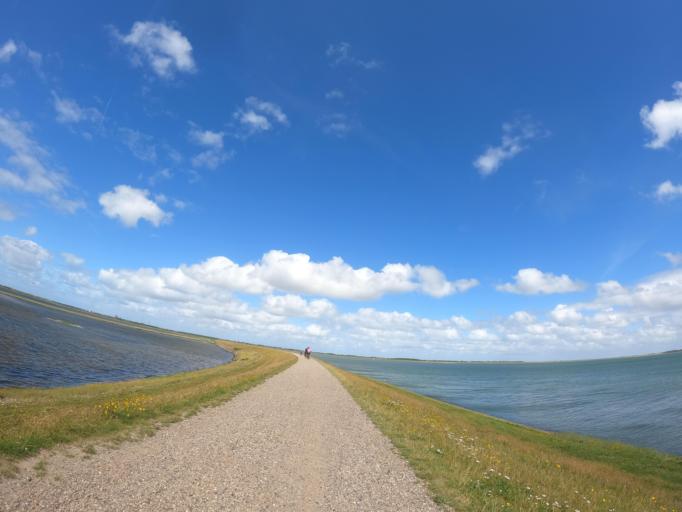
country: DE
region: Schleswig-Holstein
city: Tinnum
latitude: 54.8653
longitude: 8.3333
